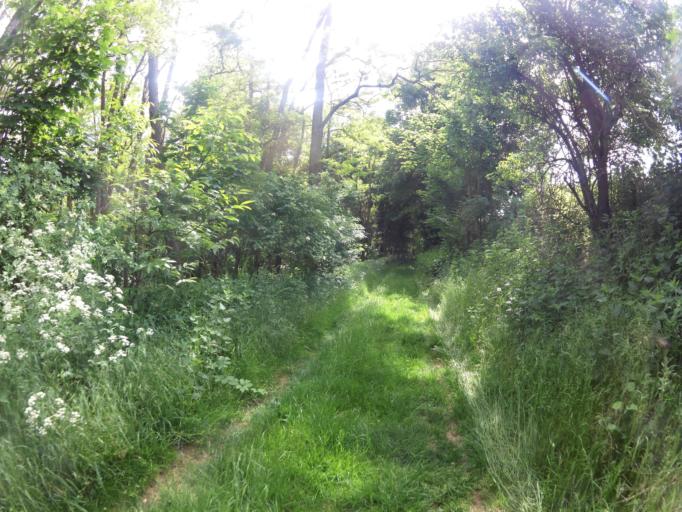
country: DE
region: Bavaria
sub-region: Regierungsbezirk Unterfranken
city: Ochsenfurt
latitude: 49.6617
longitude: 10.0342
